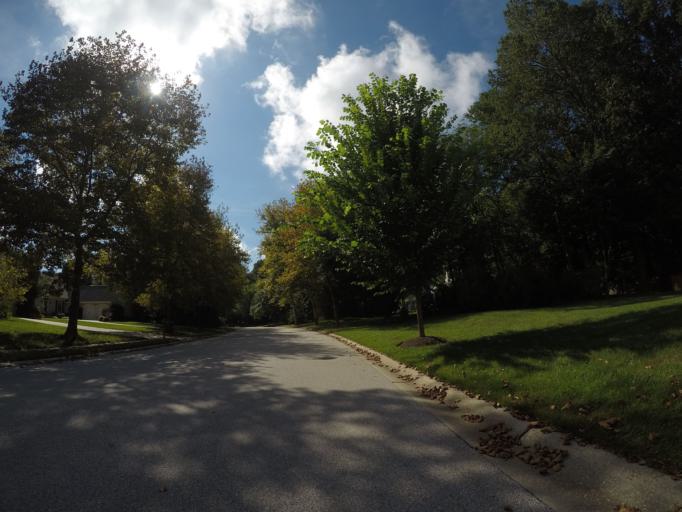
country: US
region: Maryland
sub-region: Howard County
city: Columbia
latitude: 39.2578
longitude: -76.8682
